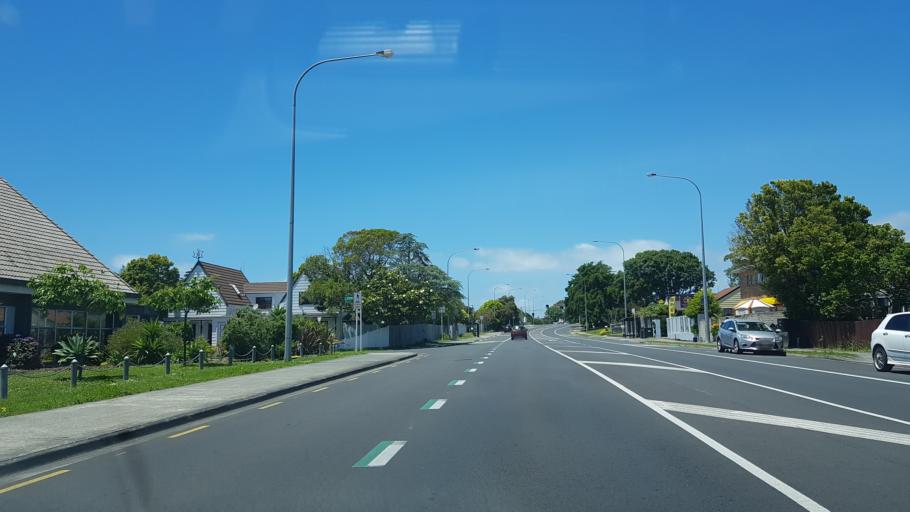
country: NZ
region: Auckland
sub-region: Auckland
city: North Shore
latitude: -36.7946
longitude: 174.7519
